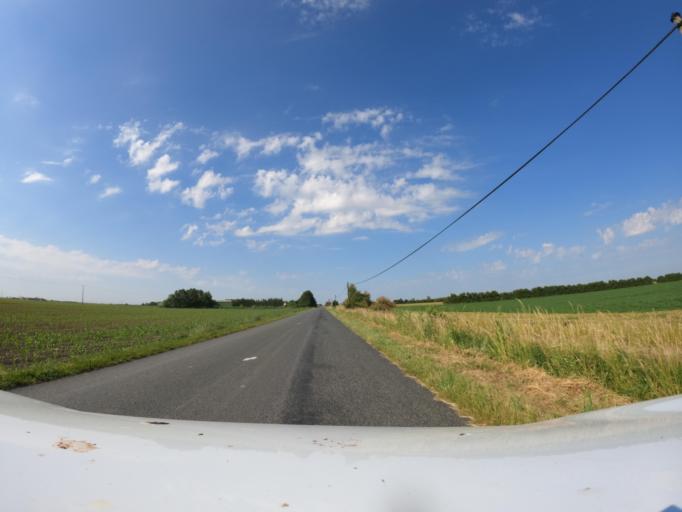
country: FR
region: Pays de la Loire
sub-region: Departement de la Vendee
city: Champagne-les-Marais
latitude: 46.3583
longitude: -1.1156
